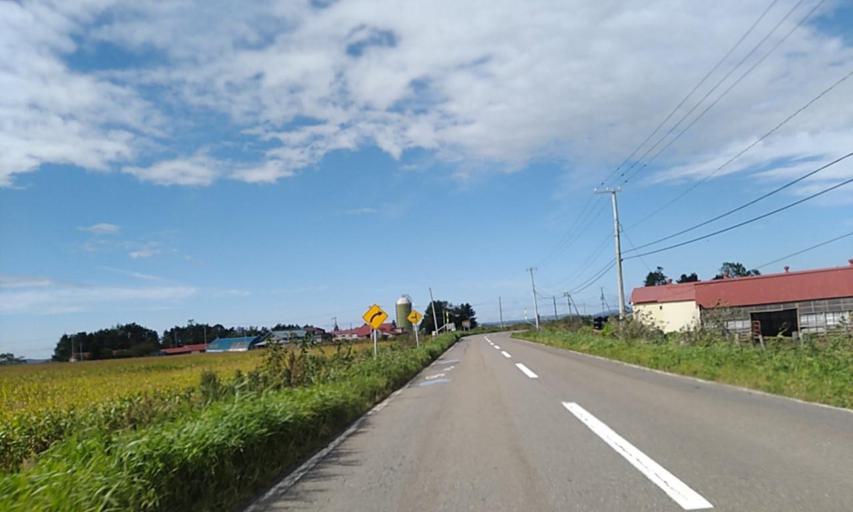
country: JP
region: Hokkaido
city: Obihiro
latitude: 42.7214
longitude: 143.6334
